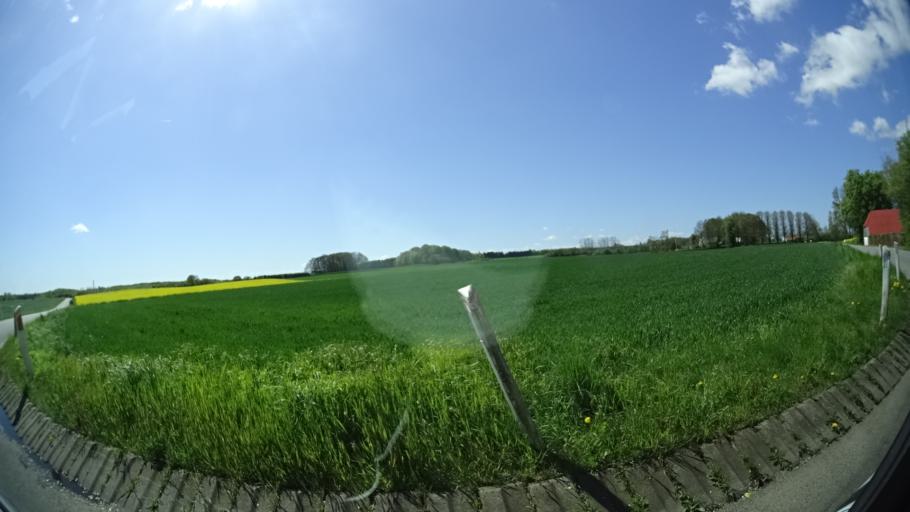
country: DK
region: Central Jutland
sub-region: Skanderborg Kommune
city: Horning
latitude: 56.1152
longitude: 10.0251
